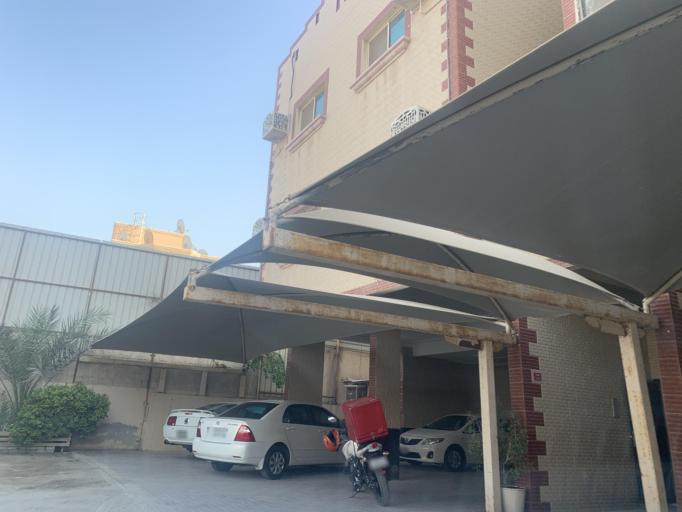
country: BH
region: Manama
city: Jidd Hafs
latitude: 26.2122
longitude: 50.5320
